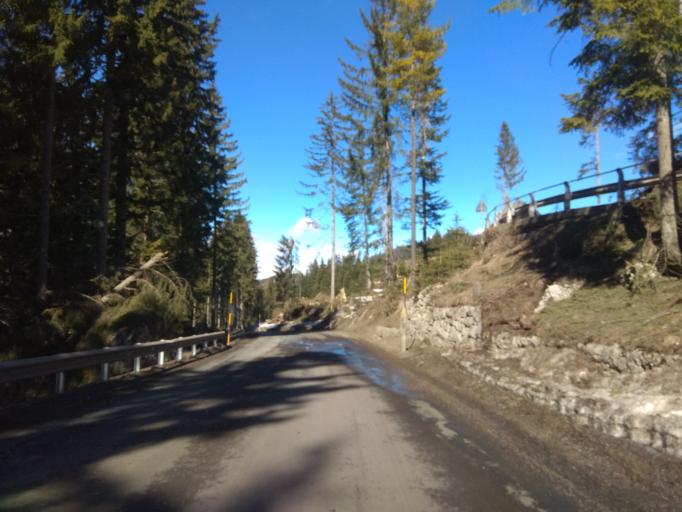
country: IT
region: Trentino-Alto Adige
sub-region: Bolzano
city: Nova Levante
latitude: 46.4111
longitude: 11.5667
